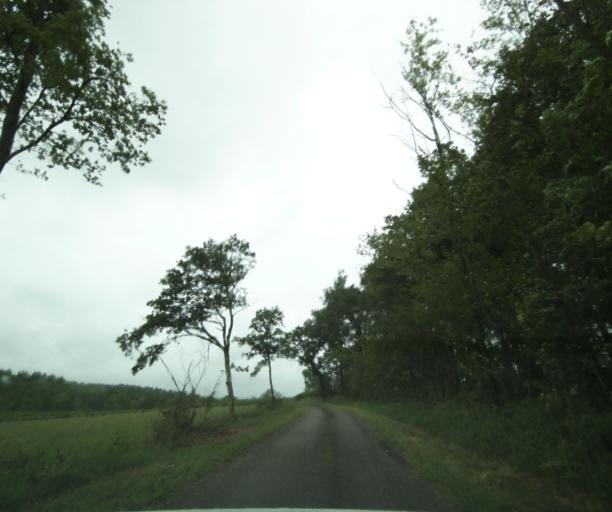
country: FR
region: Bourgogne
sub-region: Departement de Saone-et-Loire
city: Saint-Vallier
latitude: 46.4993
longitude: 4.4565
